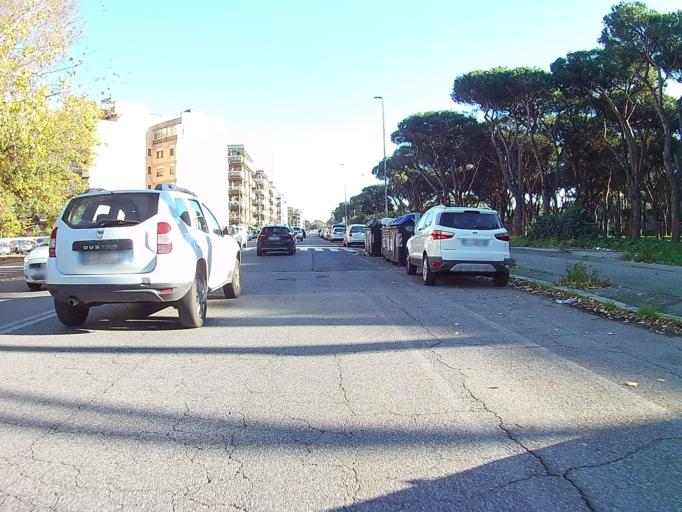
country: IT
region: Latium
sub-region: Citta metropolitana di Roma Capitale
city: Lido di Ostia
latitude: 41.7337
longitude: 12.2987
